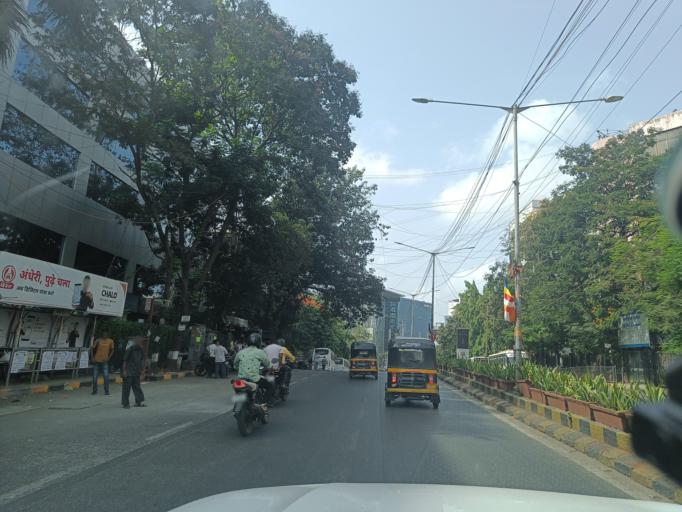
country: IN
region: Maharashtra
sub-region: Mumbai Suburban
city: Powai
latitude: 19.1210
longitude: 72.8706
